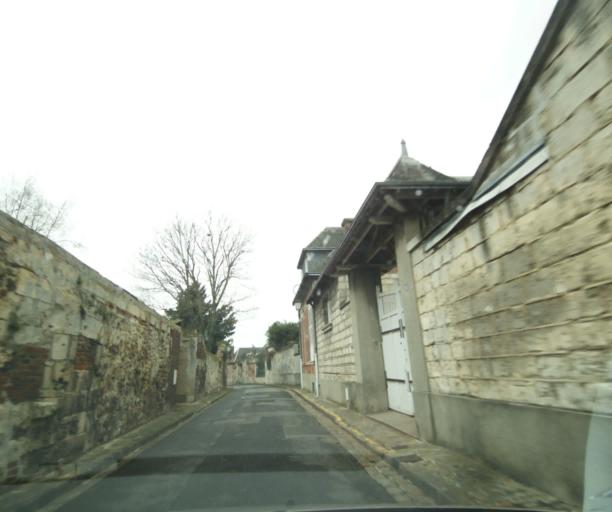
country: FR
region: Picardie
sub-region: Departement de l'Oise
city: Noyon
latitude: 49.5827
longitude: 3.0017
